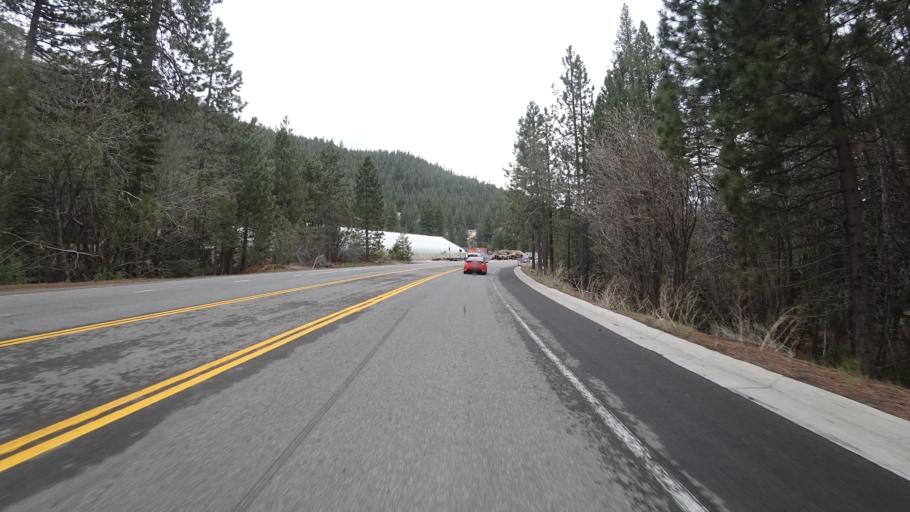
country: US
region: Nevada
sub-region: Washoe County
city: Incline Village
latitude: 39.2386
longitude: -119.9288
